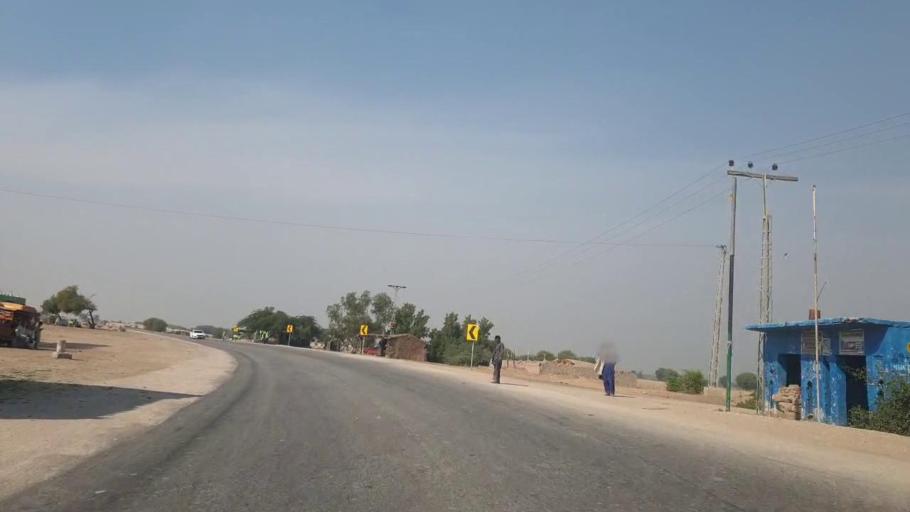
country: PK
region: Sindh
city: Sann
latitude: 25.9850
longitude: 68.1826
